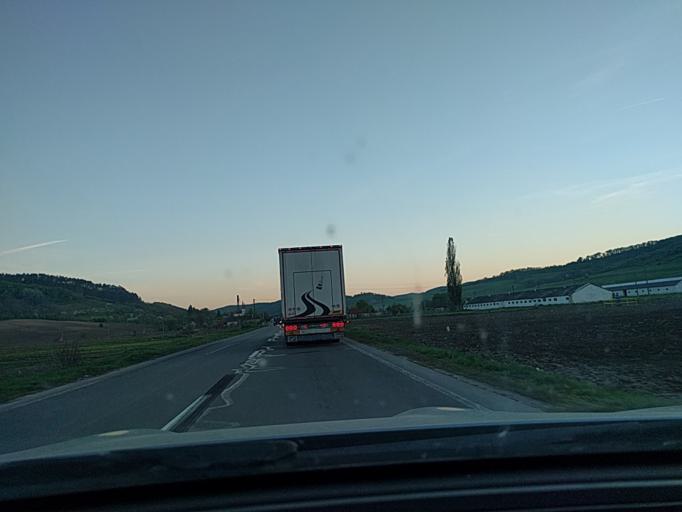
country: RO
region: Mures
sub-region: Comuna Balauseri
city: Chendu
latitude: 46.3625
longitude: 24.7208
